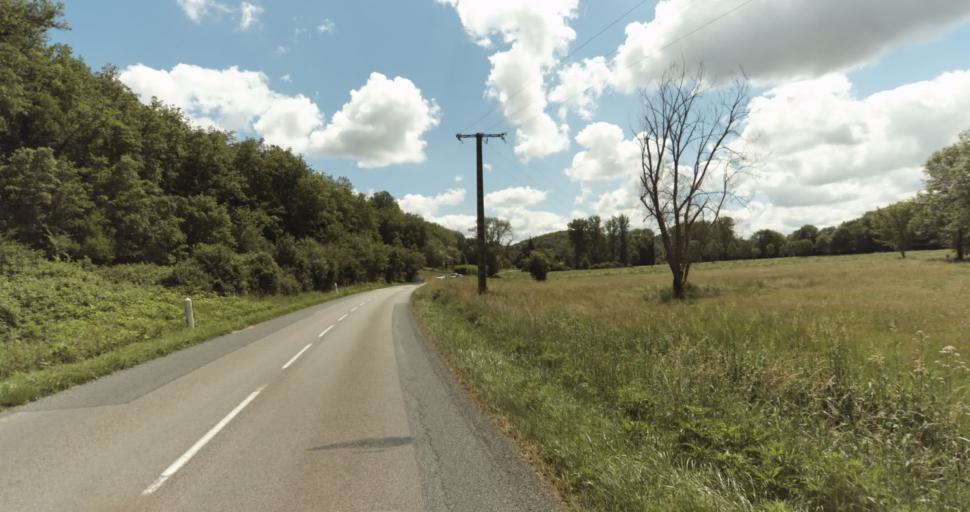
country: FR
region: Aquitaine
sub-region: Departement de la Dordogne
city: Beaumont-du-Perigord
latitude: 44.7987
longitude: 0.7477
